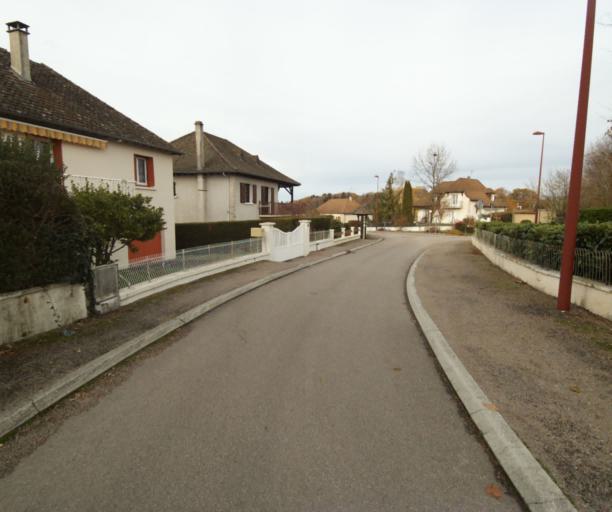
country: FR
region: Limousin
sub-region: Departement de la Correze
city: Sainte-Fortunade
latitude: 45.2139
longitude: 1.7683
